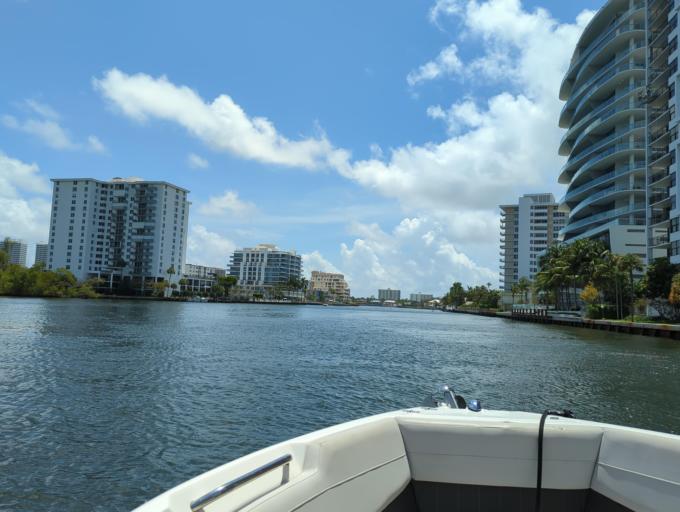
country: US
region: Florida
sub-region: Broward County
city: Sunrise
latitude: 26.1366
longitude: -80.1088
